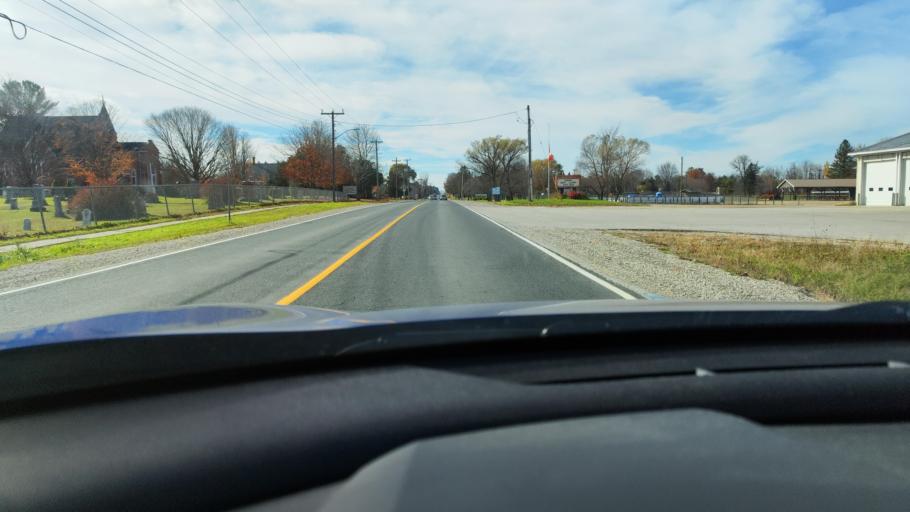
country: CA
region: Ontario
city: Angus
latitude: 44.3592
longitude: -79.9676
